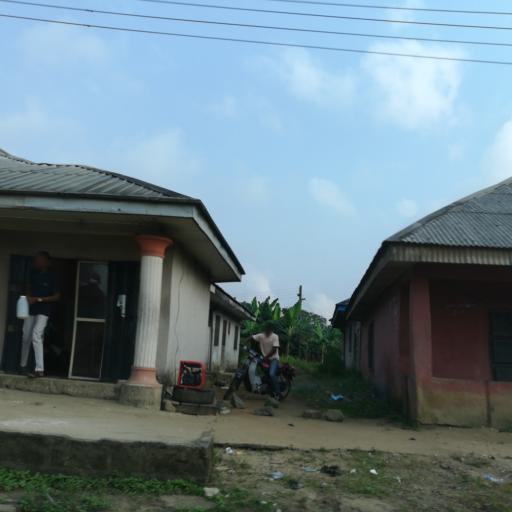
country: NG
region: Rivers
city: Okrika
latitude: 4.7814
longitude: 7.1507
